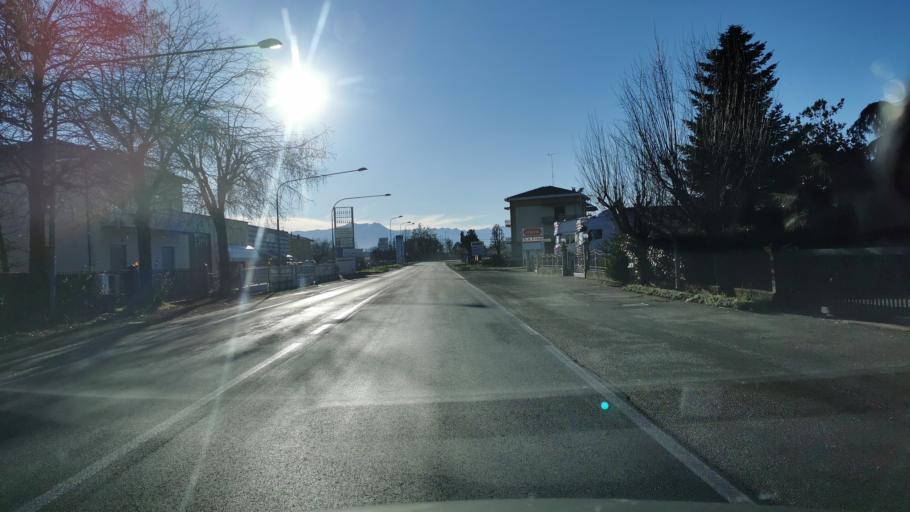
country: IT
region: Piedmont
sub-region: Provincia di Cuneo
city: Carru
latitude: 44.4761
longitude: 7.8635
